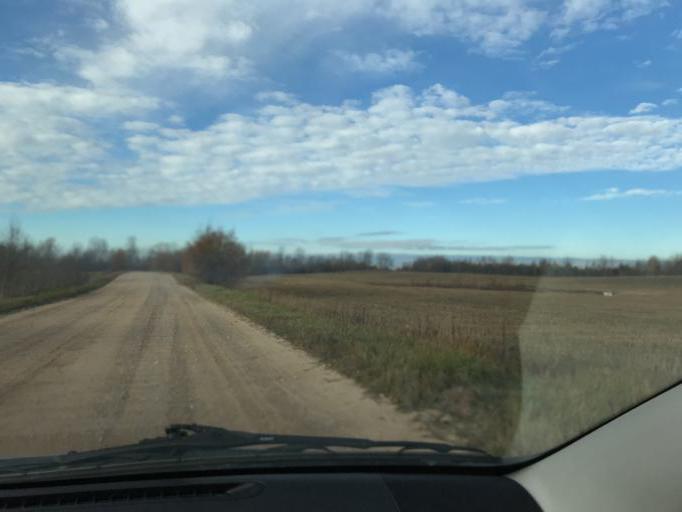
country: BY
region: Vitebsk
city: Haradok
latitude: 55.4538
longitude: 30.0298
